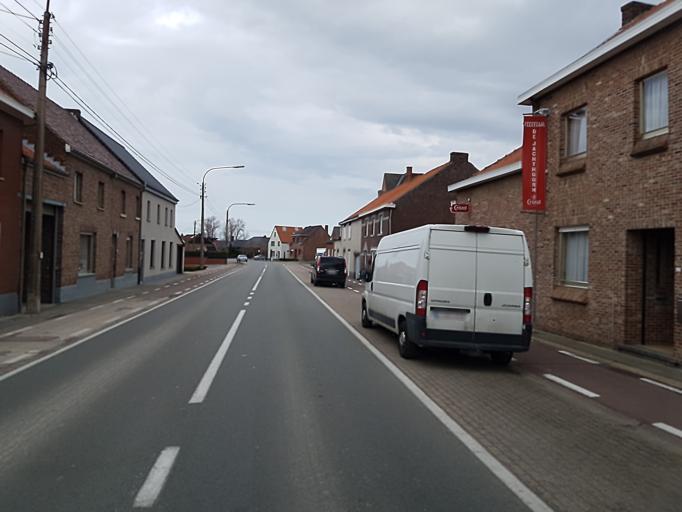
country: BE
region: Flanders
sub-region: Provincie Limburg
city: Alken
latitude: 50.8385
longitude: 5.2594
